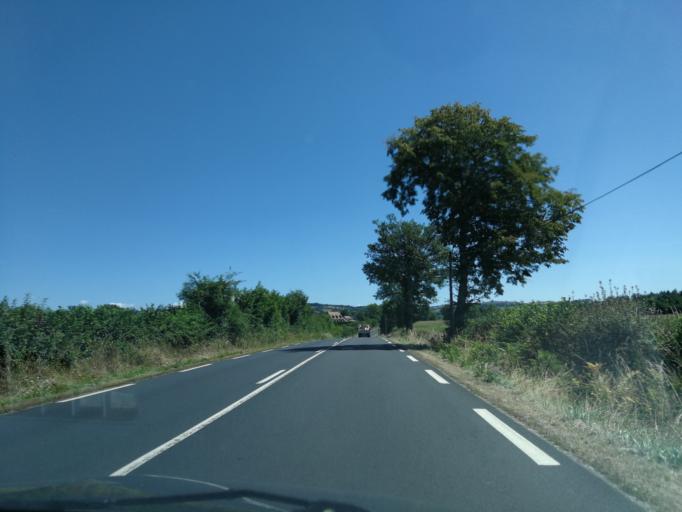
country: FR
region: Auvergne
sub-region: Departement du Cantal
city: Ytrac
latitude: 44.9338
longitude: 2.3716
